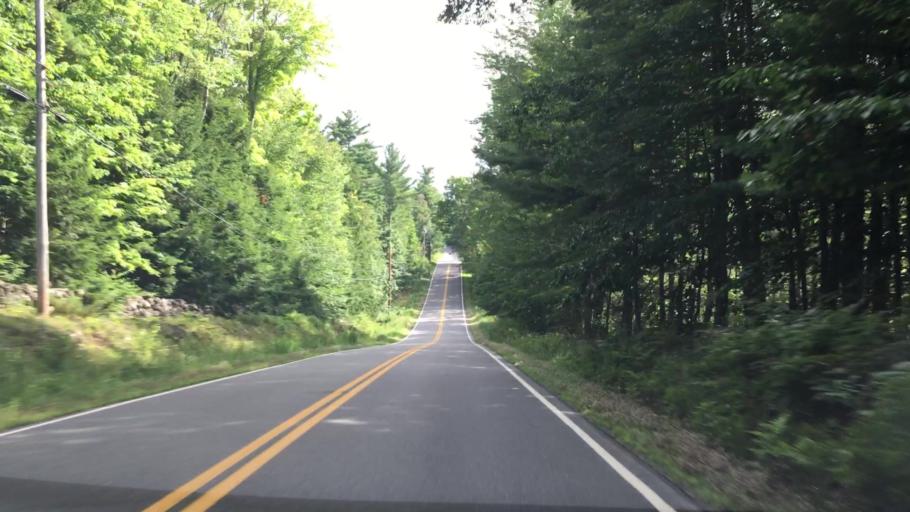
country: US
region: Maine
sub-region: Waldo County
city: Belfast
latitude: 44.3871
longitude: -69.0336
